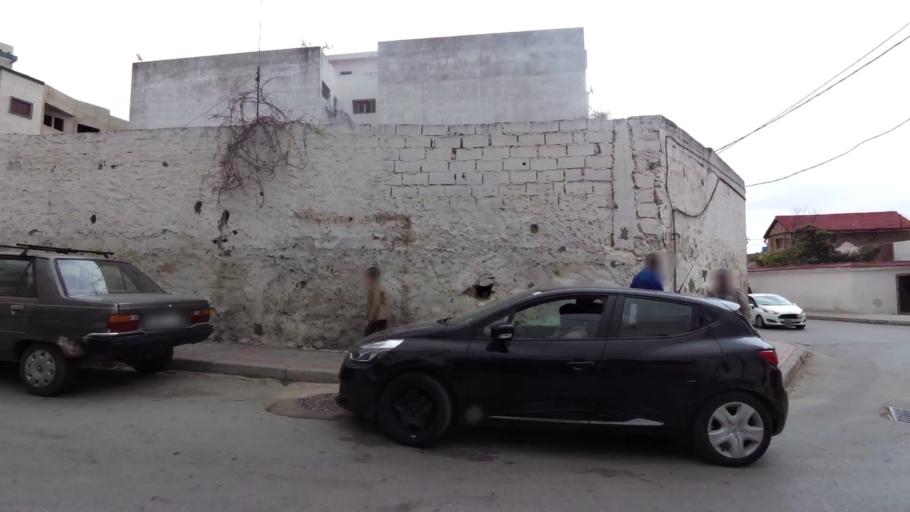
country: MA
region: Tanger-Tetouan
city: Tetouan
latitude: 35.5657
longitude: -5.3721
